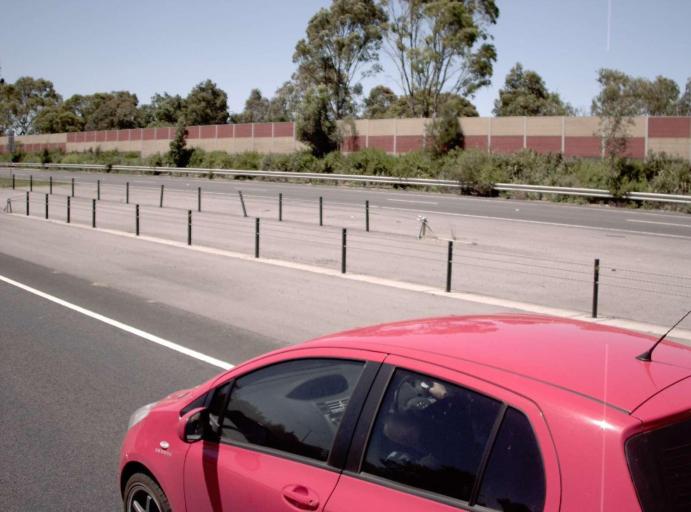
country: AU
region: Victoria
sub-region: Casey
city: Berwick
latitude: -38.0480
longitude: 145.3485
